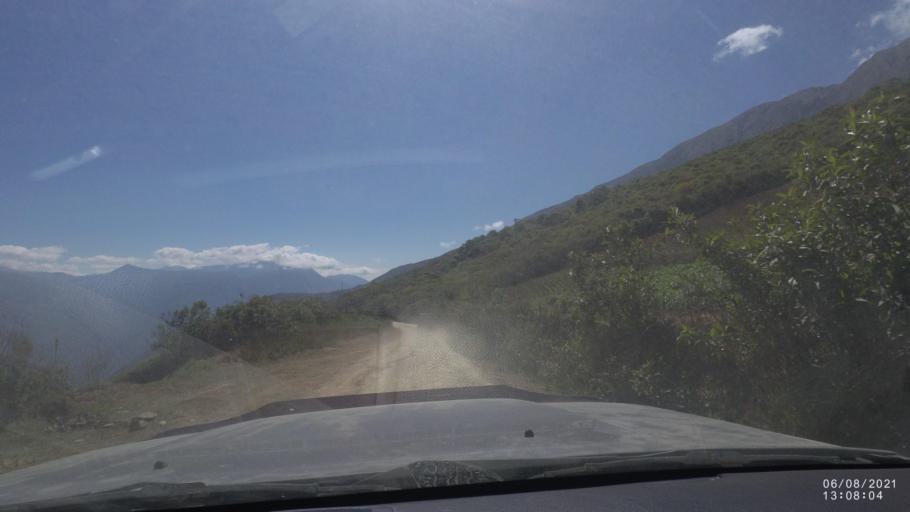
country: BO
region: La Paz
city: Quime
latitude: -16.7303
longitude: -66.7057
